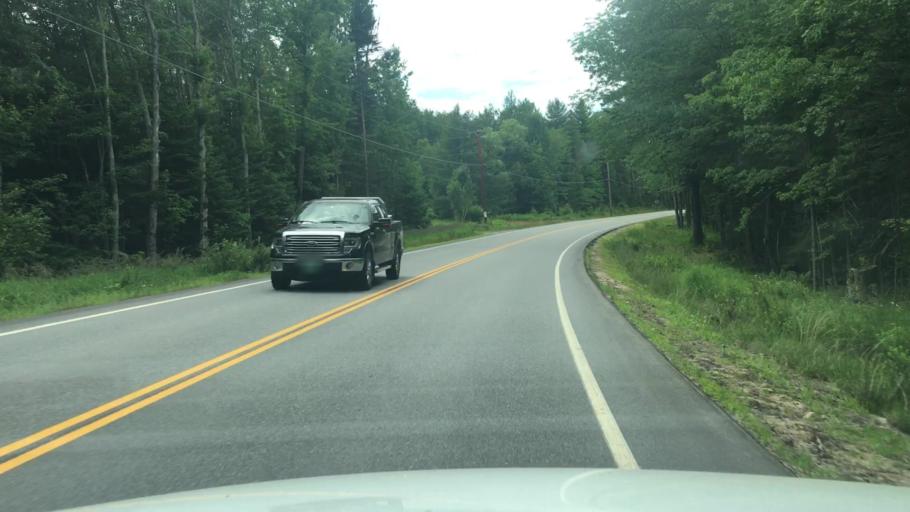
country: US
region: Maine
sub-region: Oxford County
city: West Paris
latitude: 44.3654
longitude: -70.4875
